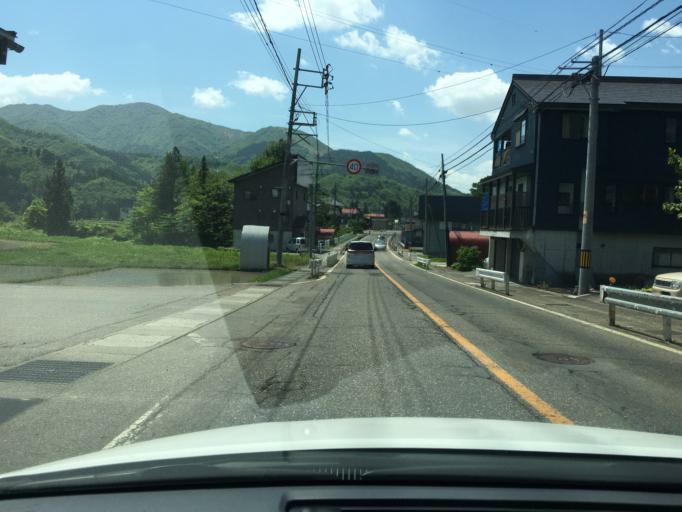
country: JP
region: Niigata
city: Tochio-honcho
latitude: 37.3146
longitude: 139.0140
